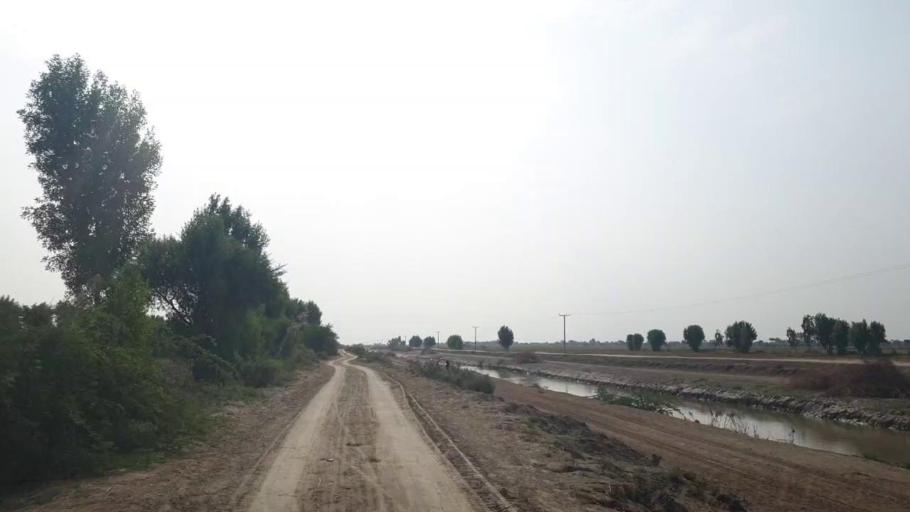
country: PK
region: Sindh
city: Badin
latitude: 24.7536
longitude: 68.7617
